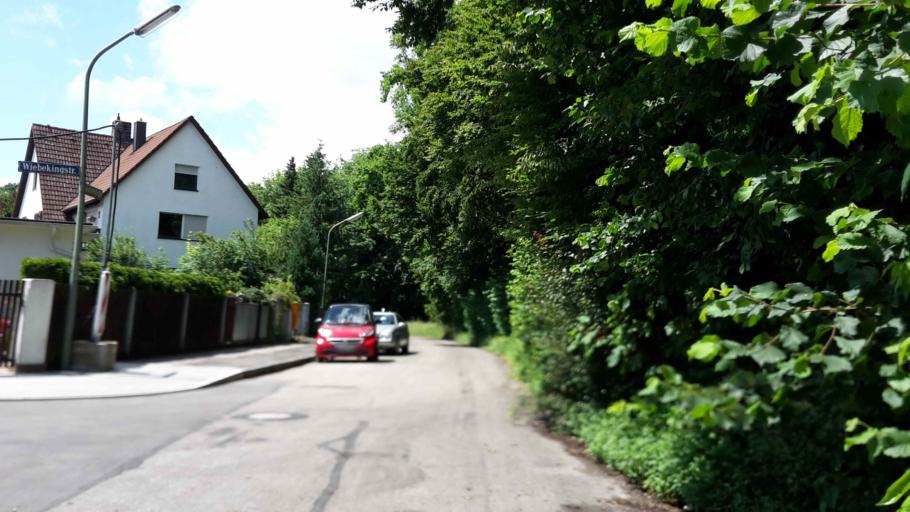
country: DE
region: Bavaria
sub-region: Upper Bavaria
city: Karlsfeld
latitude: 48.1869
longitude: 11.4787
